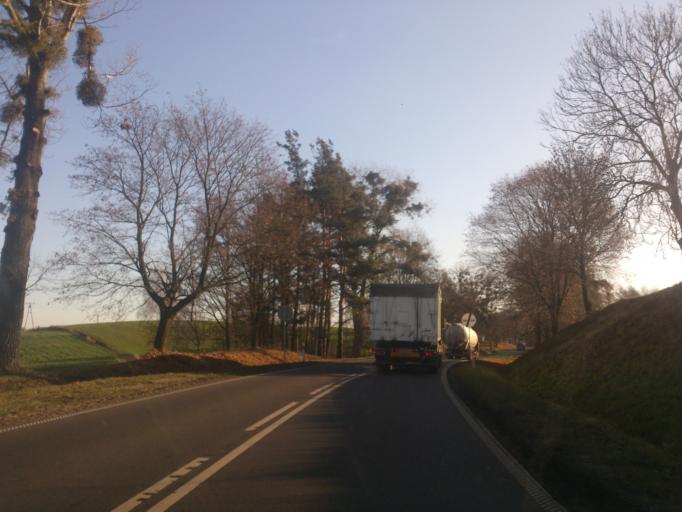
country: PL
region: Kujawsko-Pomorskie
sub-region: Powiat golubsko-dobrzynski
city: Golub-Dobrzyn
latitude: 53.1095
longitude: 19.1093
